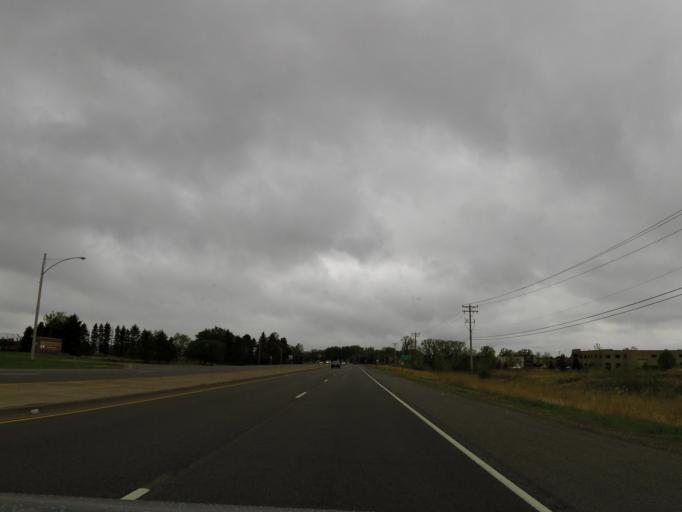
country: US
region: Minnesota
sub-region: Washington County
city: Lake Elmo
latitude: 45.0309
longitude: -92.8519
